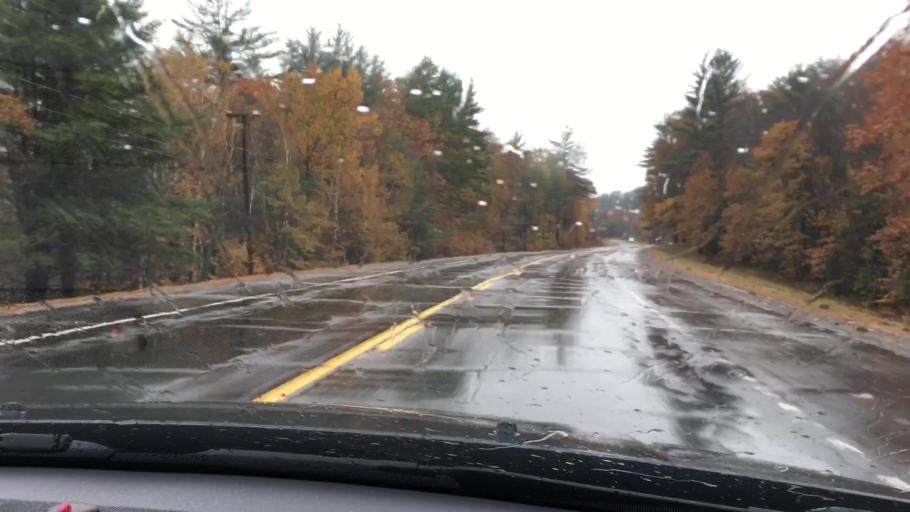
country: US
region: New Hampshire
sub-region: Grafton County
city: Ashland
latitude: 43.7104
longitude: -71.6263
